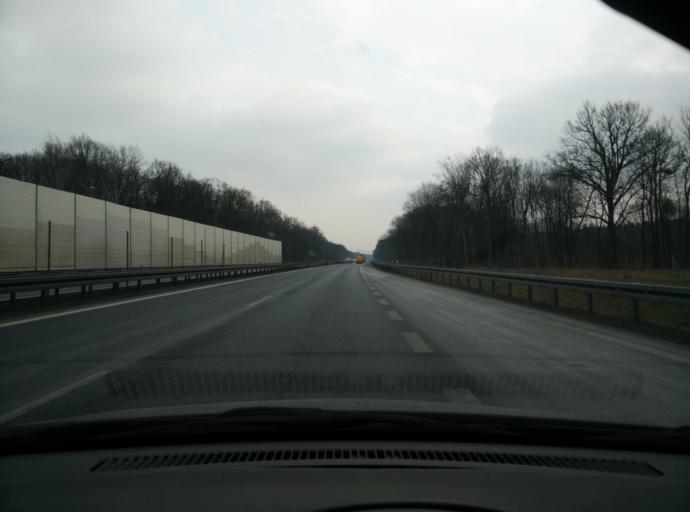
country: PL
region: Greater Poland Voivodeship
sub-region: Powiat poznanski
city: Kornik
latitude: 52.2939
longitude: 17.0534
